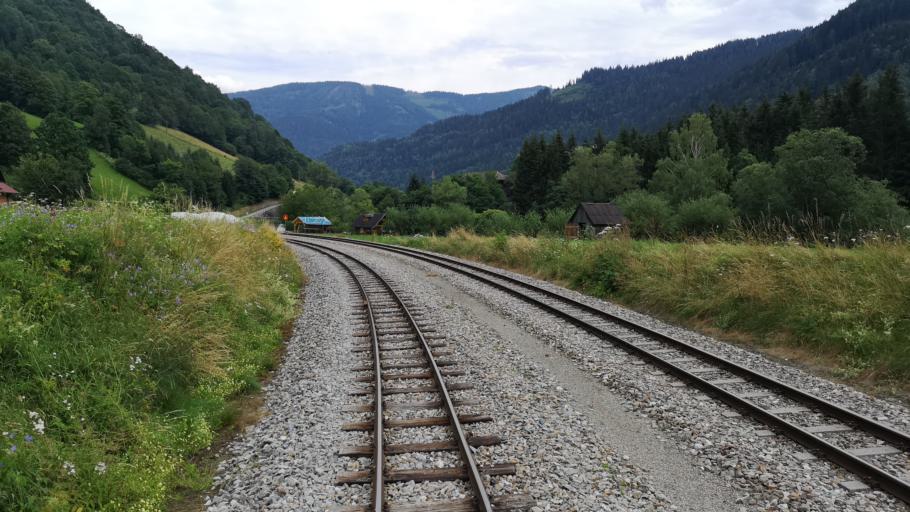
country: AT
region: Salzburg
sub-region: Politischer Bezirk Tamsweg
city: Ramingstein
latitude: 47.0696
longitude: 13.8795
